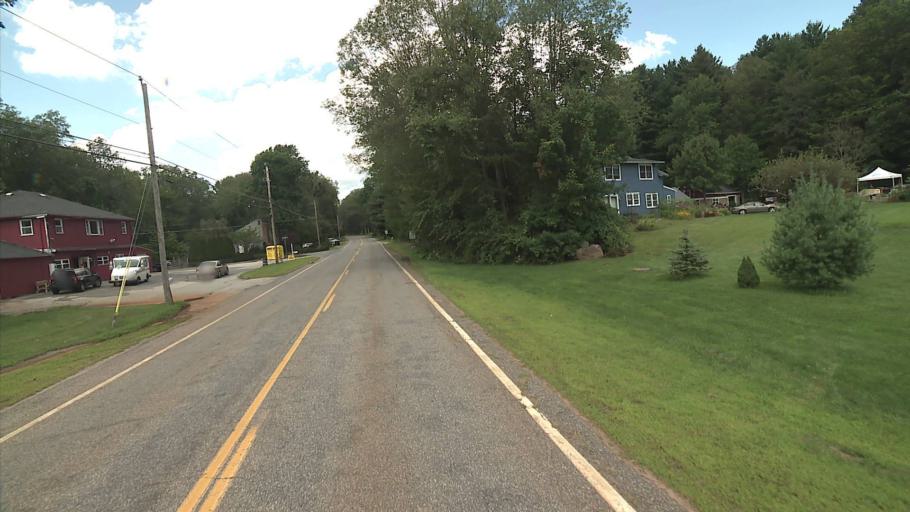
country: US
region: Connecticut
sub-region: Tolland County
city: Stafford
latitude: 41.9346
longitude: -72.1930
